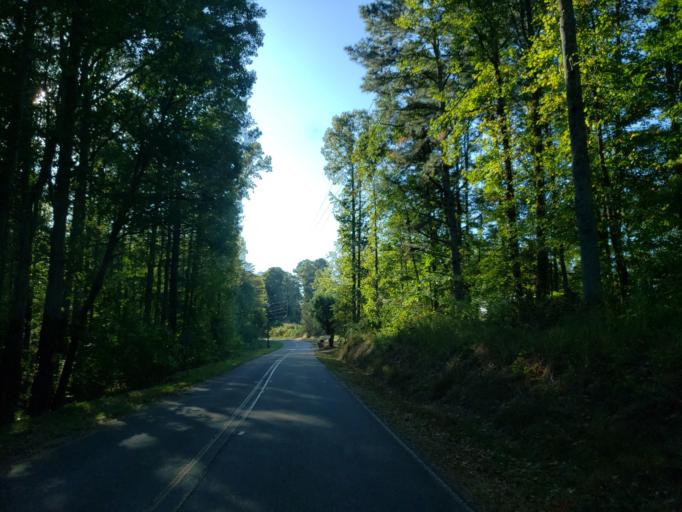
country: US
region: Georgia
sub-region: Pickens County
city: Nelson
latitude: 34.3766
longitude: -84.3882
